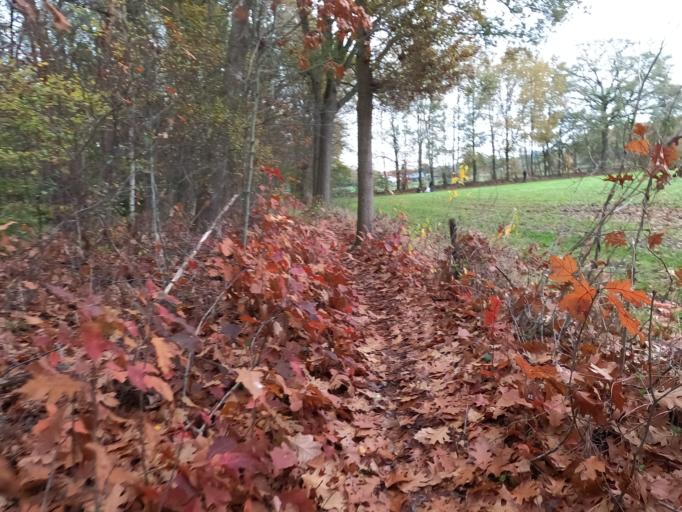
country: BE
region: Flanders
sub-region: Provincie Antwerpen
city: Nijlen
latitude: 51.1355
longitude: 4.7028
